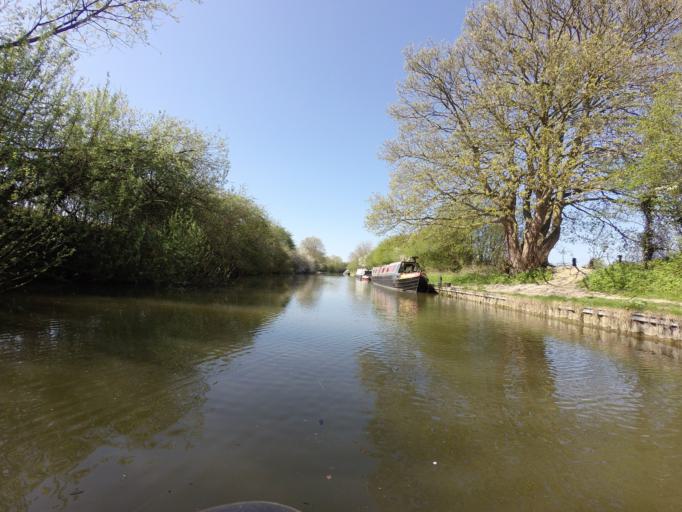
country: GB
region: England
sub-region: Hertfordshire
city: Tring
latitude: 51.7905
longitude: -0.6188
